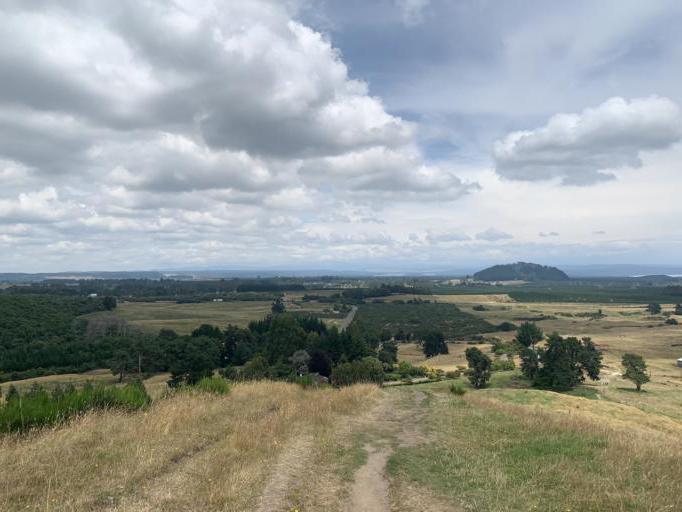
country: NZ
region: Waikato
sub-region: Taupo District
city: Taupo
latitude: -38.7013
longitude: 176.1422
